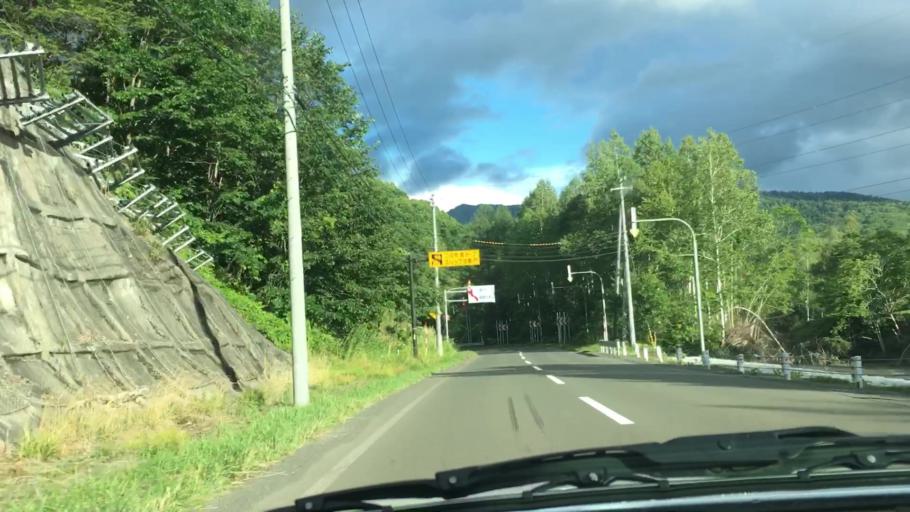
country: JP
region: Hokkaido
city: Shimo-furano
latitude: 43.1139
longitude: 142.6864
